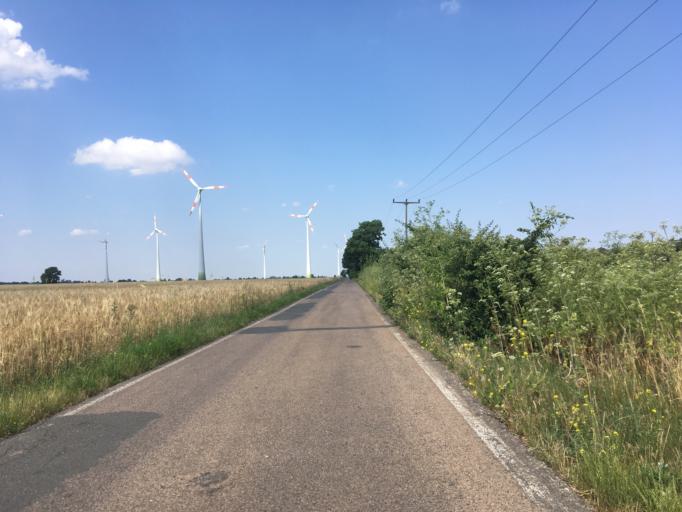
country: DE
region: Saxony-Anhalt
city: Quellendorf
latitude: 51.7832
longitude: 12.1410
